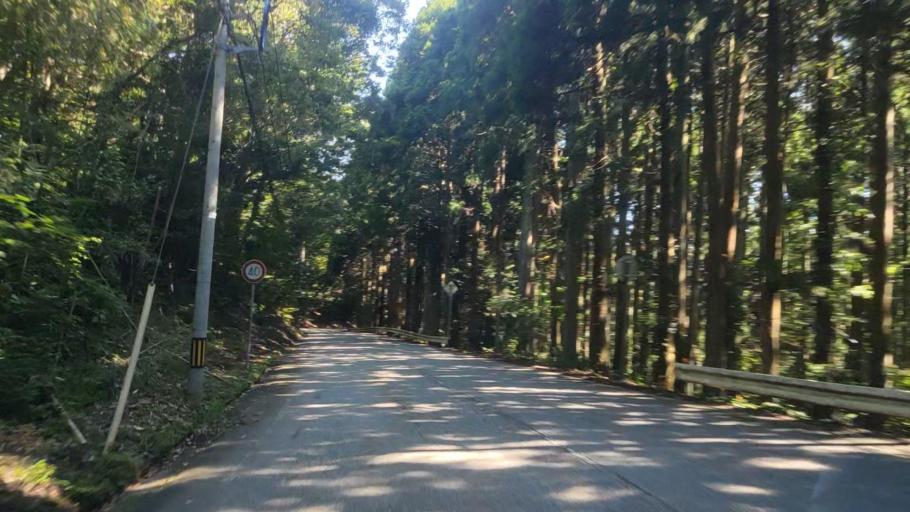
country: JP
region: Ishikawa
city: Nanao
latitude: 37.5089
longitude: 137.3377
